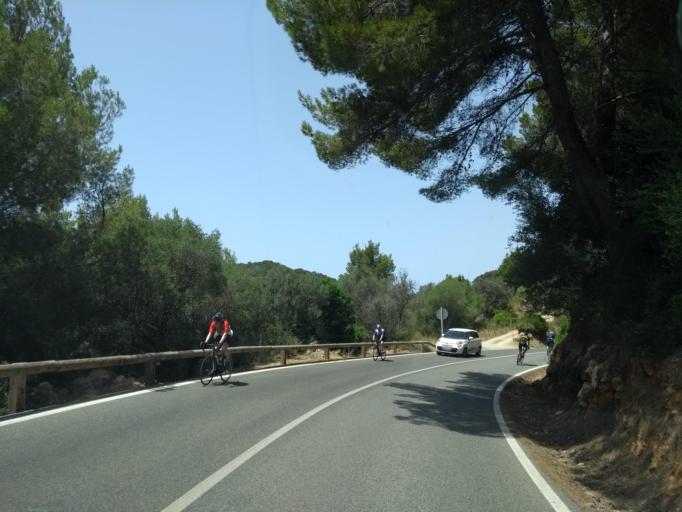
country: ES
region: Balearic Islands
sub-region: Illes Balears
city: Soller
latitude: 39.7829
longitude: 2.7114
